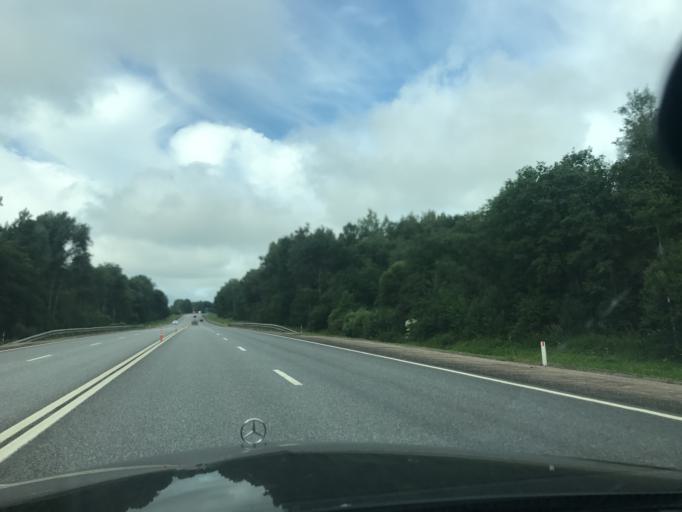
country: RU
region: Smolensk
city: Kardymovo
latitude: 55.0366
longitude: 32.4181
